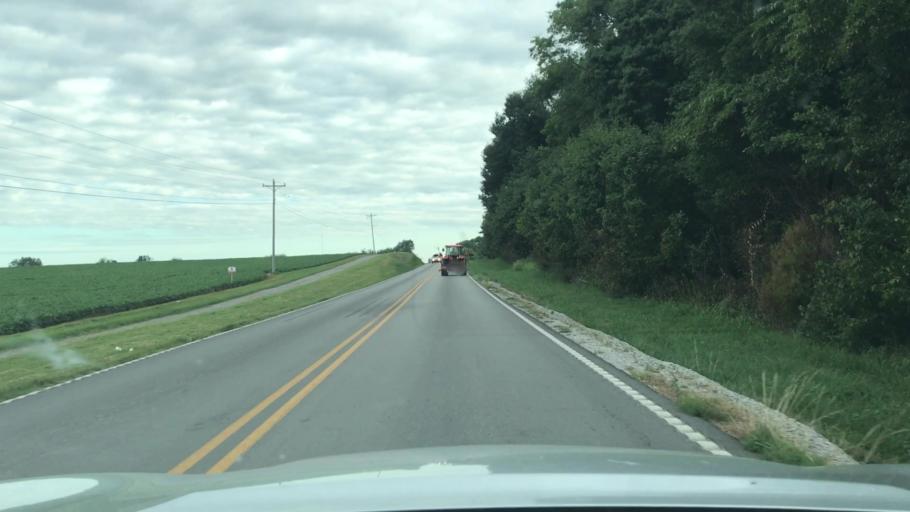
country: US
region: Kentucky
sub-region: Todd County
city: Guthrie
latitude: 36.6860
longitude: -87.2010
